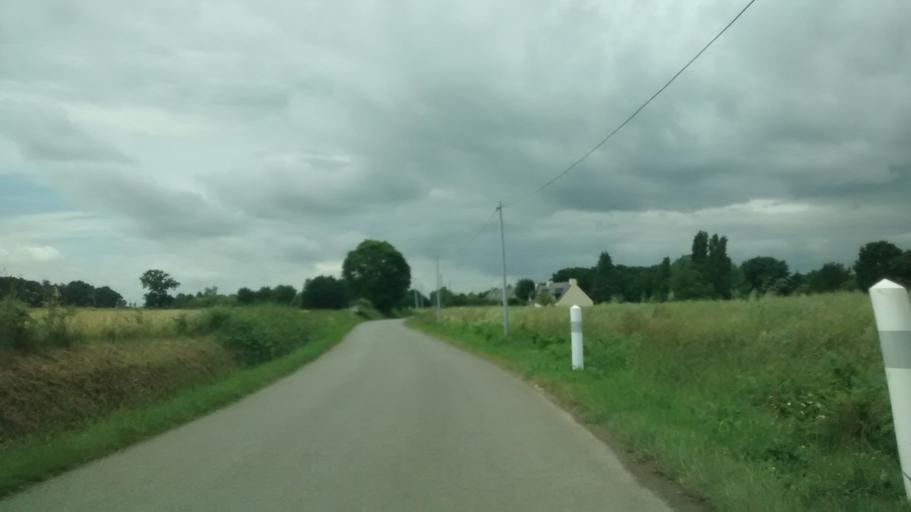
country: FR
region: Brittany
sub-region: Departement du Morbihan
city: Carentoir
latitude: 47.8060
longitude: -2.1179
